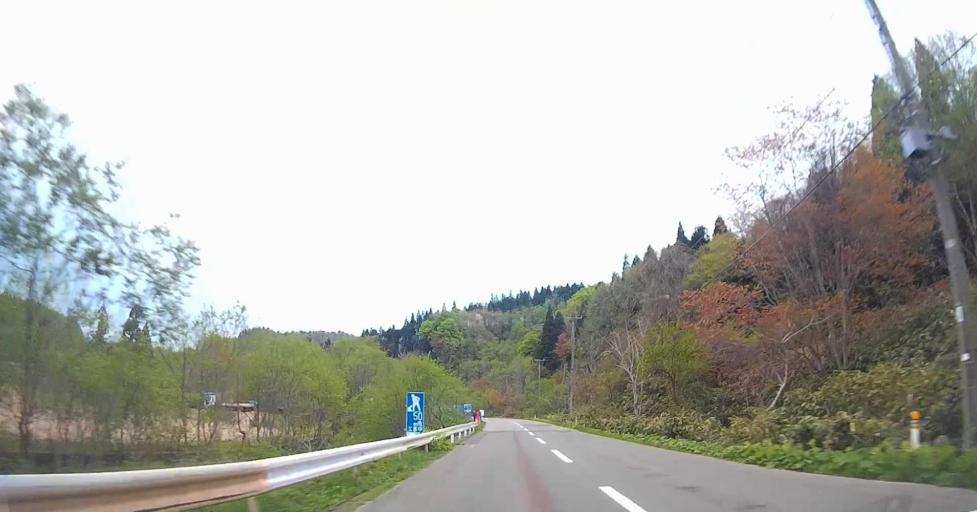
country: JP
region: Aomori
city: Goshogawara
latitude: 41.1198
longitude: 140.5235
